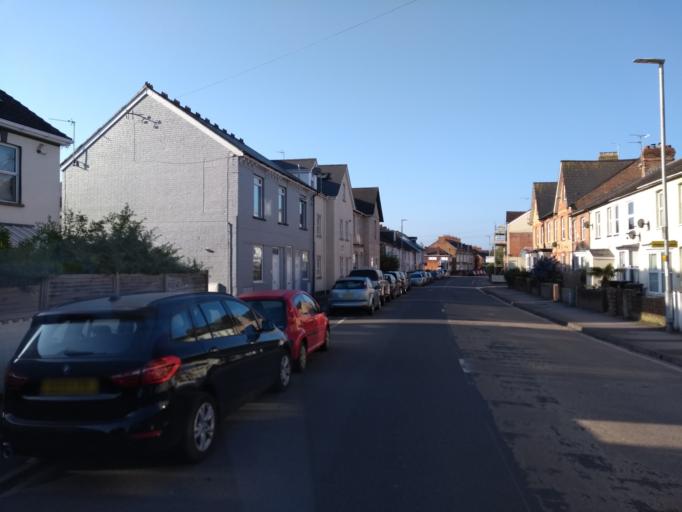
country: GB
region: England
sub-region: Somerset
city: Taunton
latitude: 51.0280
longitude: -3.1012
